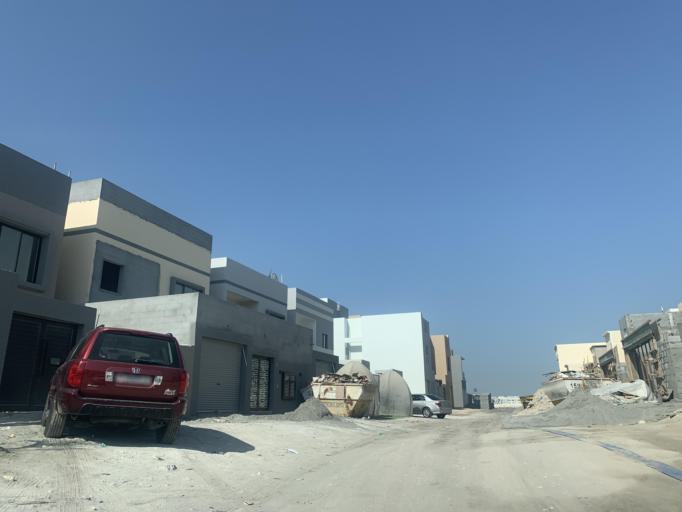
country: BH
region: Central Governorate
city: Madinat Hamad
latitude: 26.1273
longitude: 50.4857
